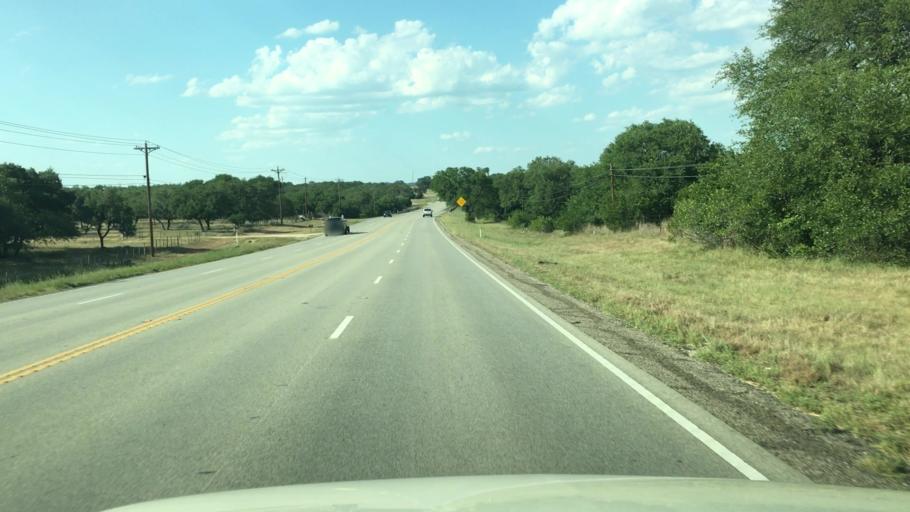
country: US
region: Texas
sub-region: Blanco County
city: Johnson City
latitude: 30.3074
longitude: -98.3942
